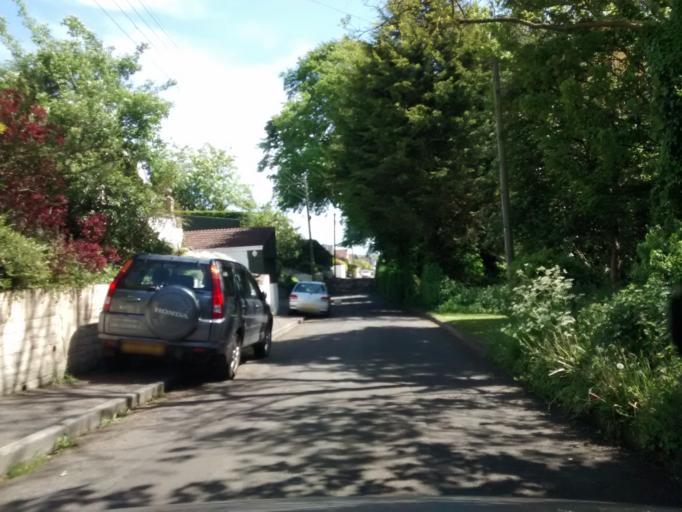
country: GB
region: England
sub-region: Bath and North East Somerset
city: Radstock
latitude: 51.2979
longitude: -2.4503
